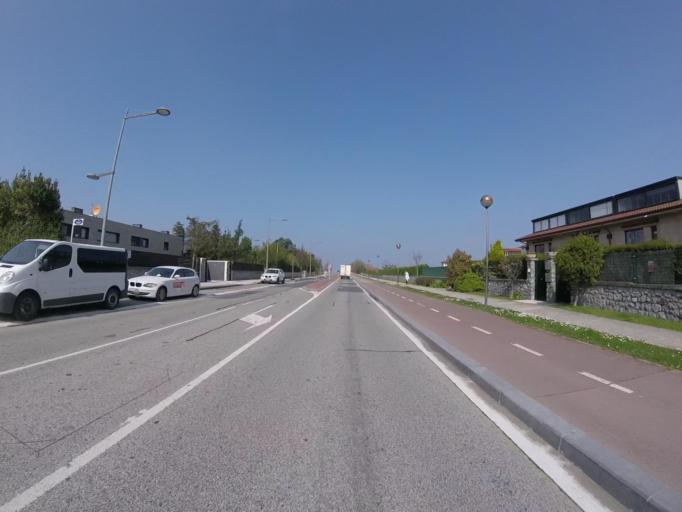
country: ES
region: Basque Country
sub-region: Provincia de Guipuzcoa
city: San Sebastian
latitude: 43.2917
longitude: -1.9908
